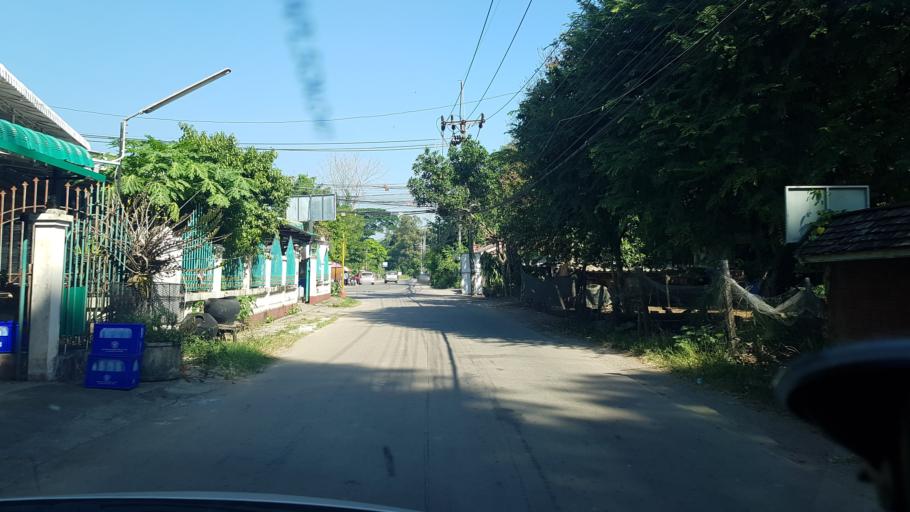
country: TH
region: Chiang Rai
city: Chiang Rai
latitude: 19.9060
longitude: 99.7936
